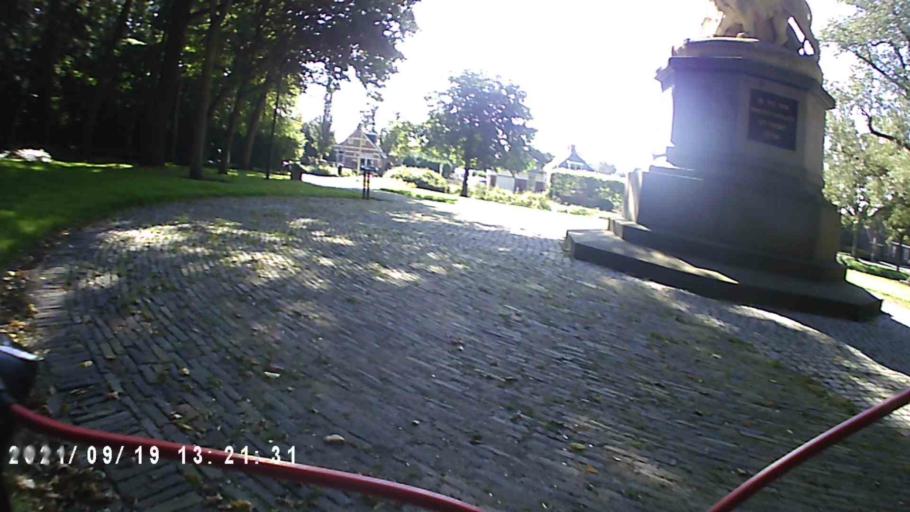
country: NL
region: Groningen
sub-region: Gemeente  Oldambt
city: Winschoten
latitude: 53.1570
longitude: 7.0030
